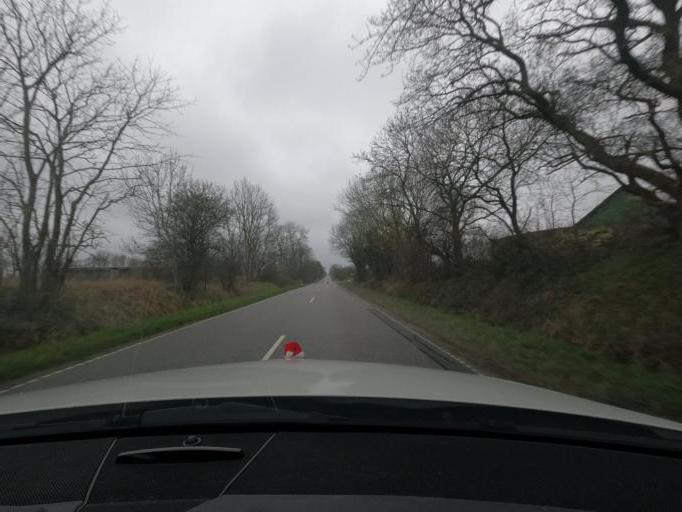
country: DK
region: South Denmark
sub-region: Haderslev Kommune
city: Starup
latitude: 55.2205
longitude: 9.6163
